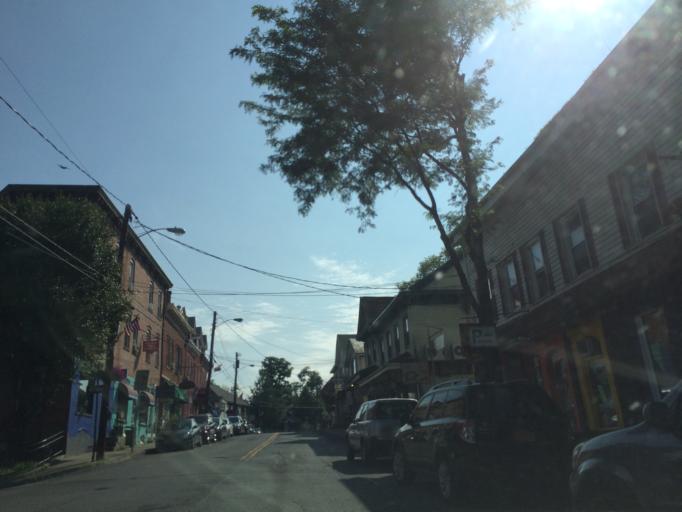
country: US
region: New York
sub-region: Ulster County
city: New Paltz
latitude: 41.7477
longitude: -74.0863
